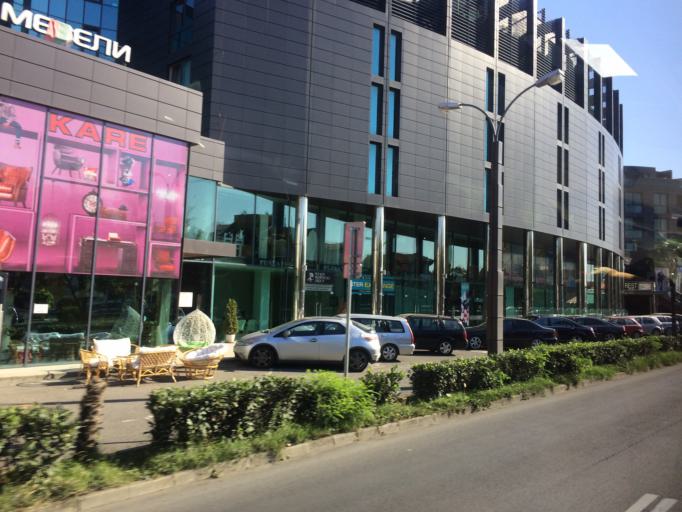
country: BG
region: Burgas
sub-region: Obshtina Nesebur
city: Sveti Vlas
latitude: 42.7088
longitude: 27.7235
